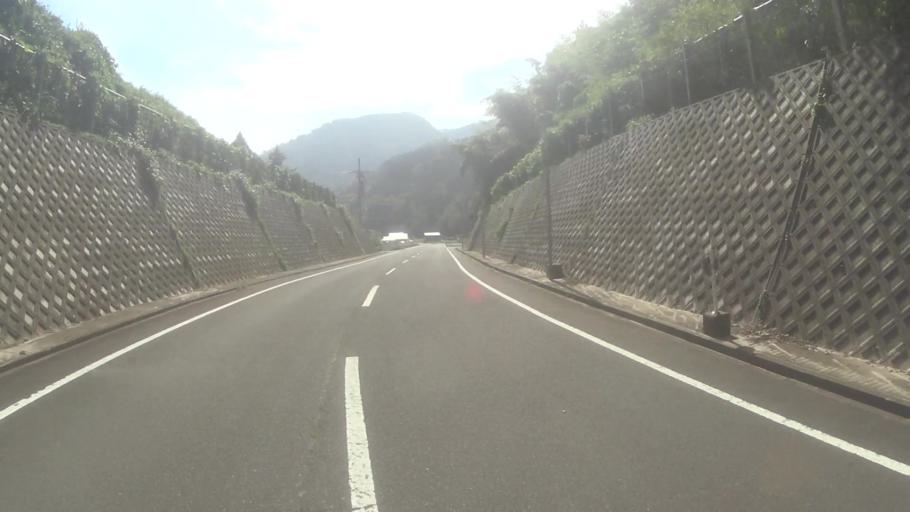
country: JP
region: Kyoto
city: Miyazu
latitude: 35.7301
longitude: 135.1637
